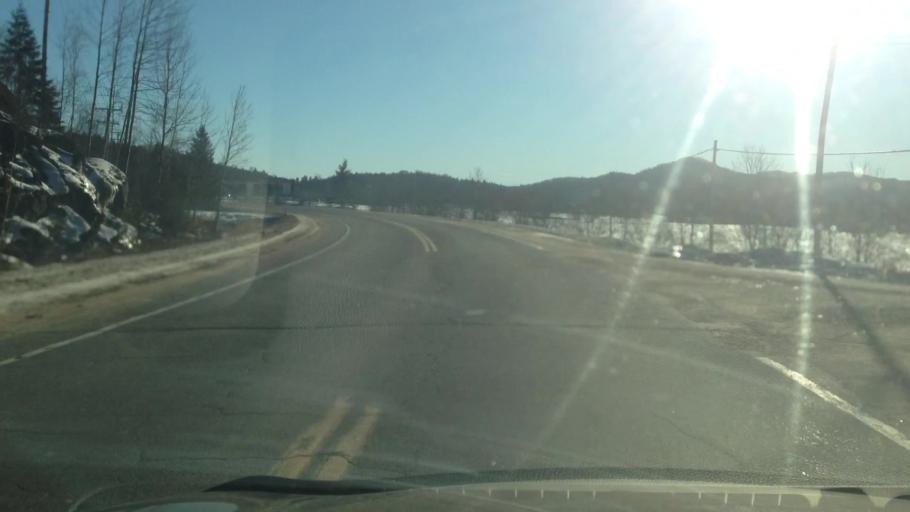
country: CA
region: Quebec
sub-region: Laurentides
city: Mont-Tremblant
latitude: 46.0722
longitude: -74.6222
